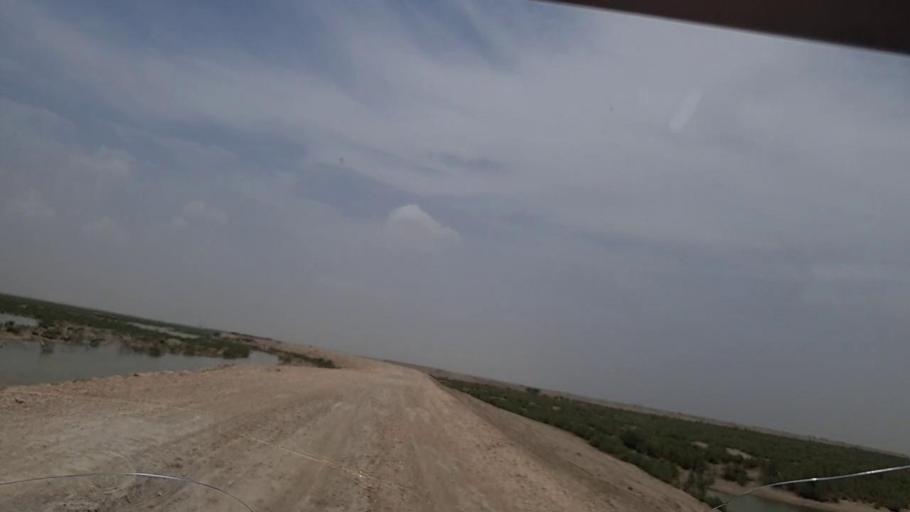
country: PK
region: Sindh
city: Bhan
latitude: 26.5072
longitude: 67.6302
